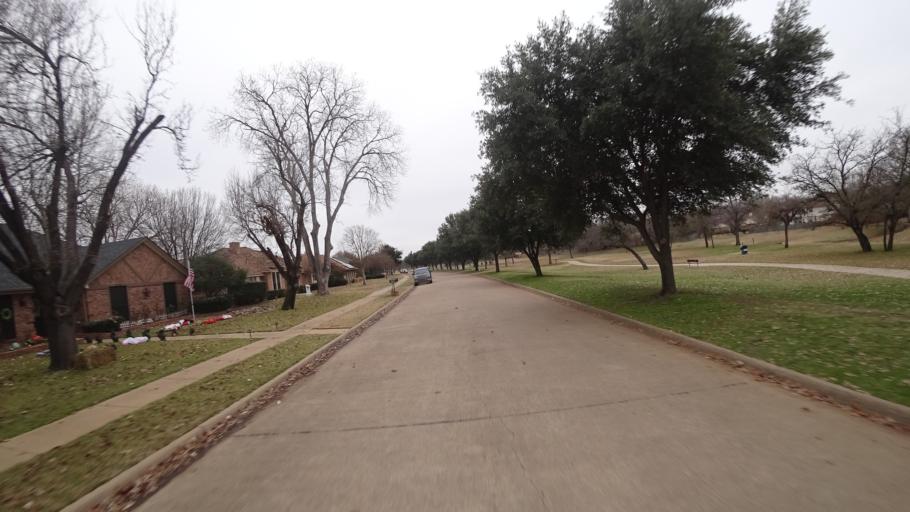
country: US
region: Texas
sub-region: Denton County
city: Highland Village
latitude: 33.0551
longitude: -97.0414
